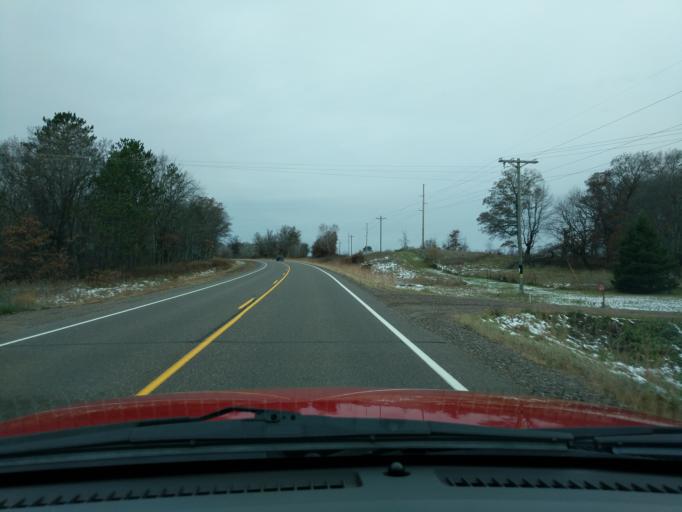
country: US
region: Wisconsin
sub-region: Washburn County
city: Shell Lake
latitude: 45.8158
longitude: -92.1259
